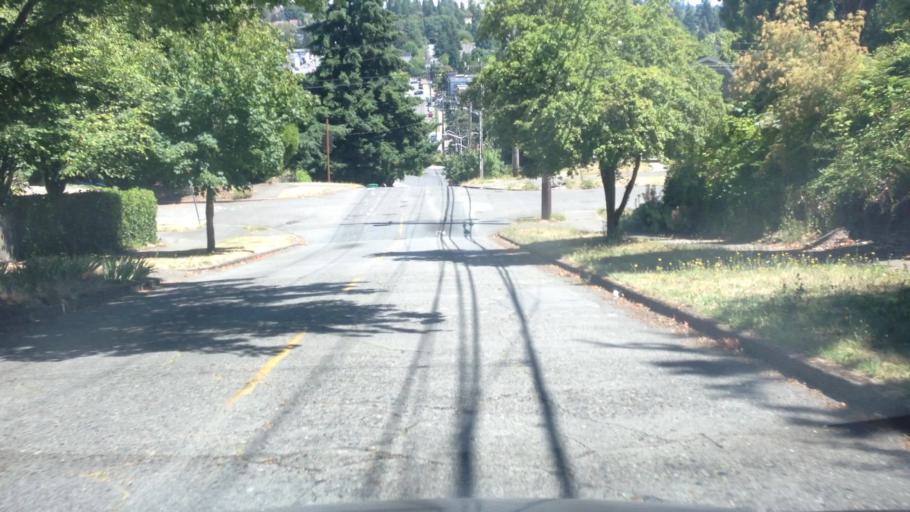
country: US
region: Washington
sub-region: King County
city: Seattle
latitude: 47.6680
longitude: -122.3061
